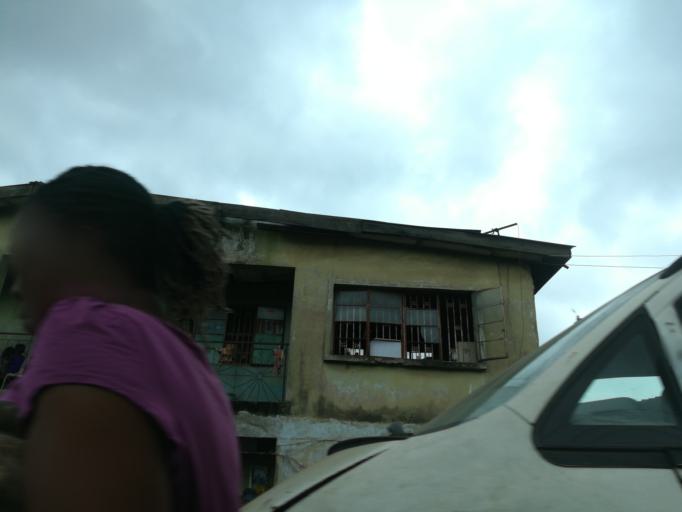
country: NG
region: Lagos
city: Oshodi
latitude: 6.5502
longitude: 3.3370
